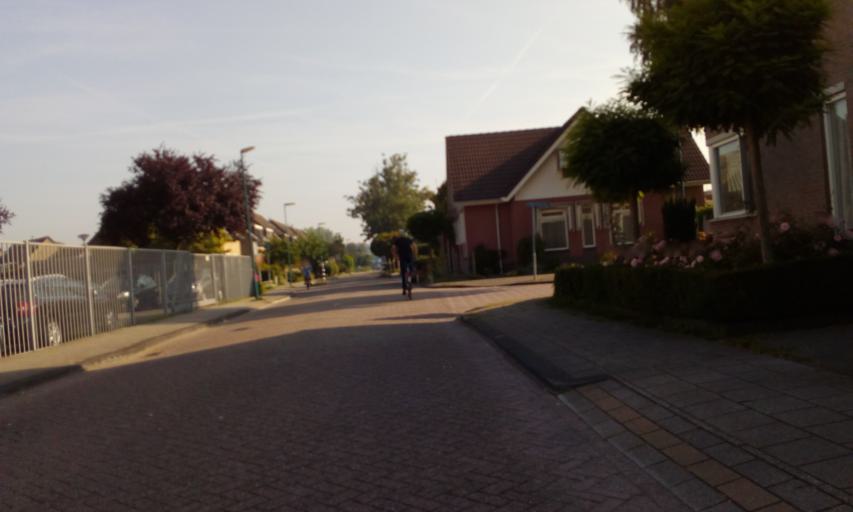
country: NL
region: South Holland
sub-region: Gemeente Zoetermeer
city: Zoetermeer
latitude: 52.0427
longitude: 4.4979
